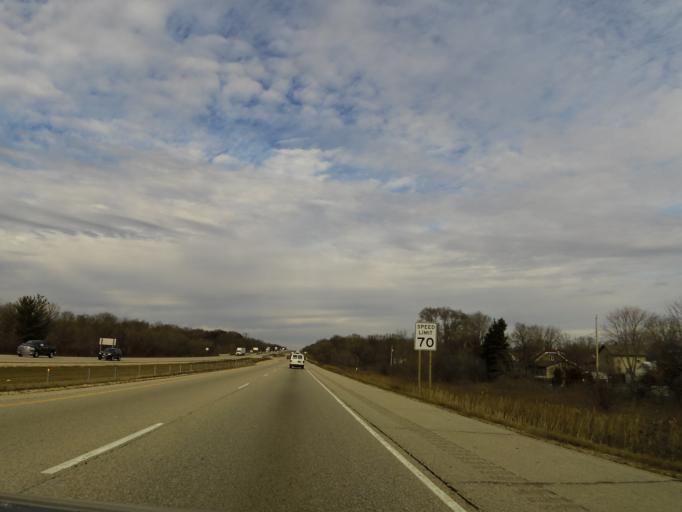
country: US
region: Wisconsin
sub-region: Rock County
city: Janesville
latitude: 42.6807
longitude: -88.9836
